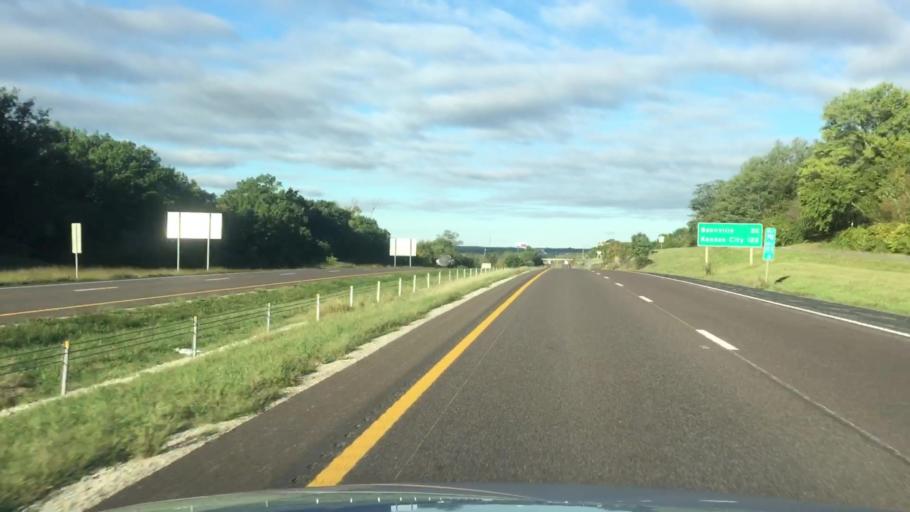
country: US
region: Missouri
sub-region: Boone County
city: Columbia
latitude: 38.9700
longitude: -92.3876
